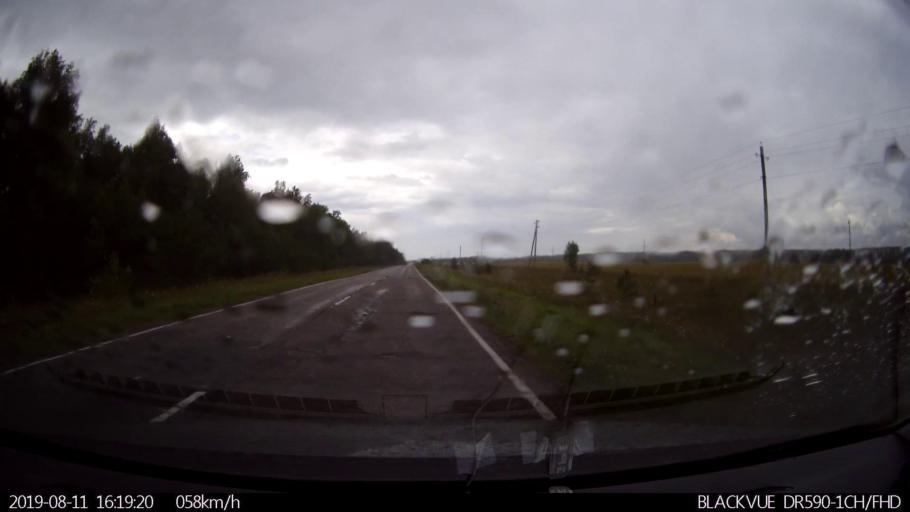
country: RU
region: Ulyanovsk
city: Mayna
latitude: 54.0629
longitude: 47.6079
